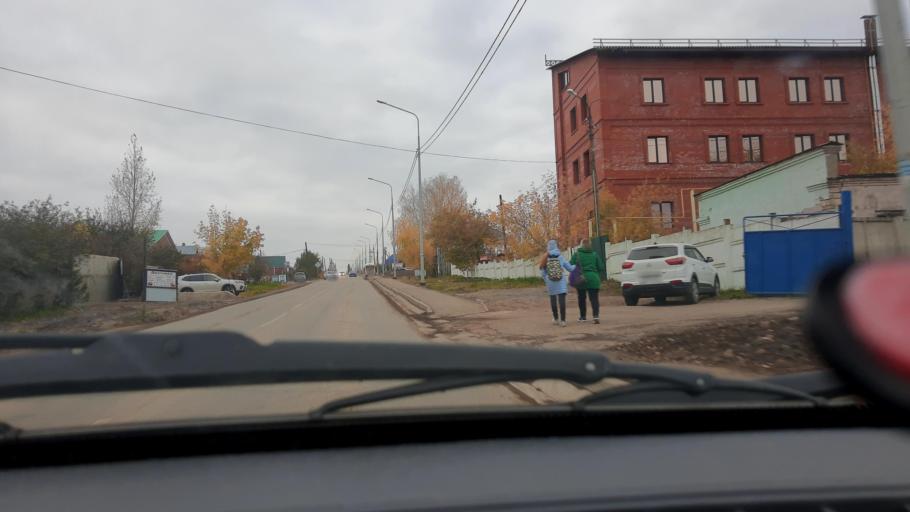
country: RU
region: Bashkortostan
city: Mikhaylovka
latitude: 54.8082
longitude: 55.8889
